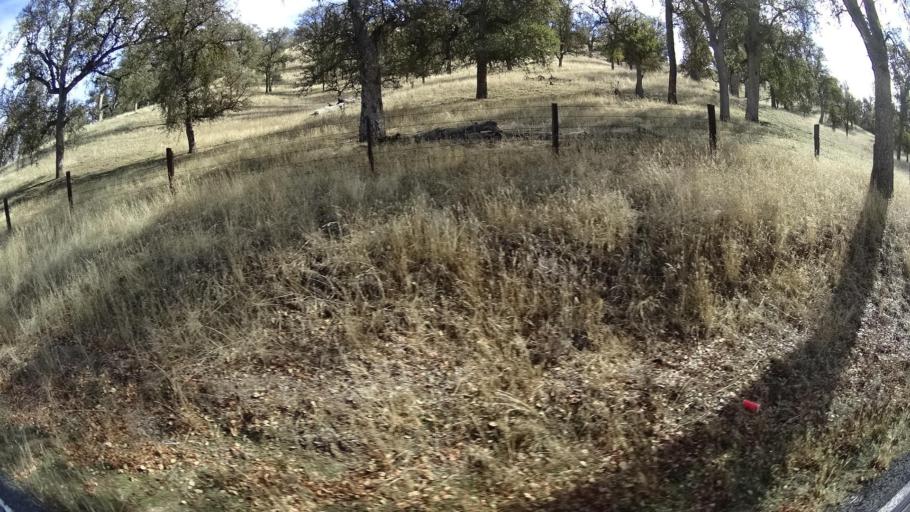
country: US
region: California
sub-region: Kern County
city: Alta Sierra
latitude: 35.6659
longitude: -118.7463
